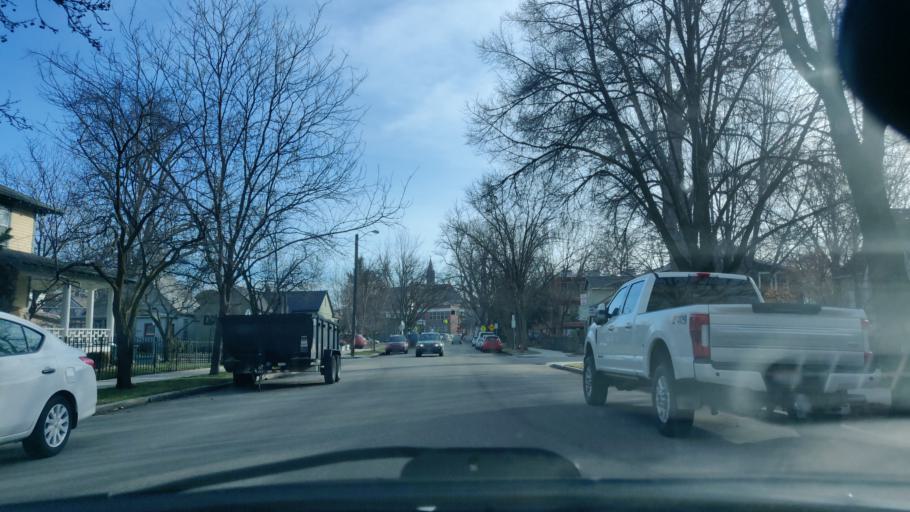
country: US
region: Idaho
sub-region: Ada County
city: Boise
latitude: 43.6244
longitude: -116.1987
